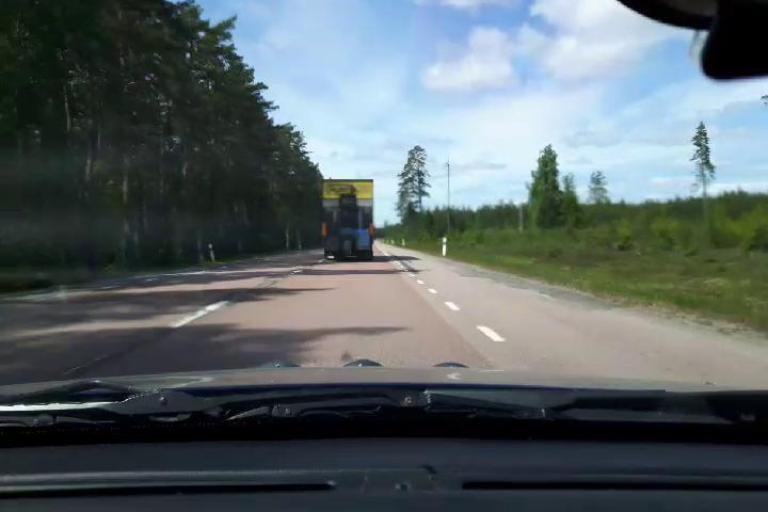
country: SE
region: Uppsala
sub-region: Osthammars Kommun
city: Bjorklinge
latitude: 60.1147
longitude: 17.5215
